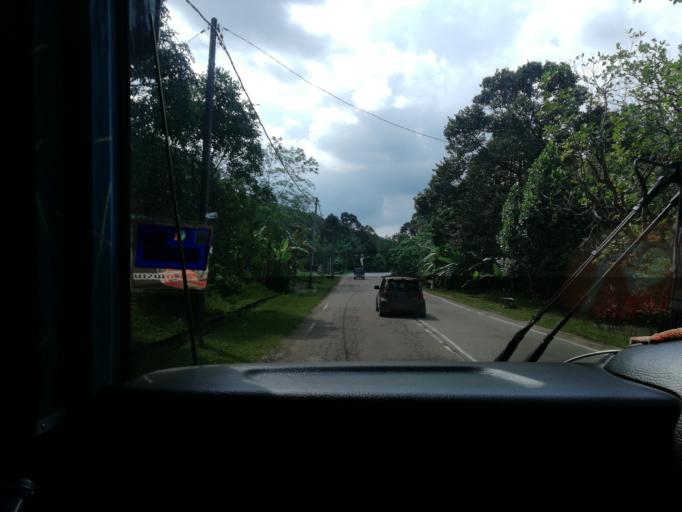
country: MY
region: Kedah
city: Kulim
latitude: 5.2960
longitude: 100.6249
